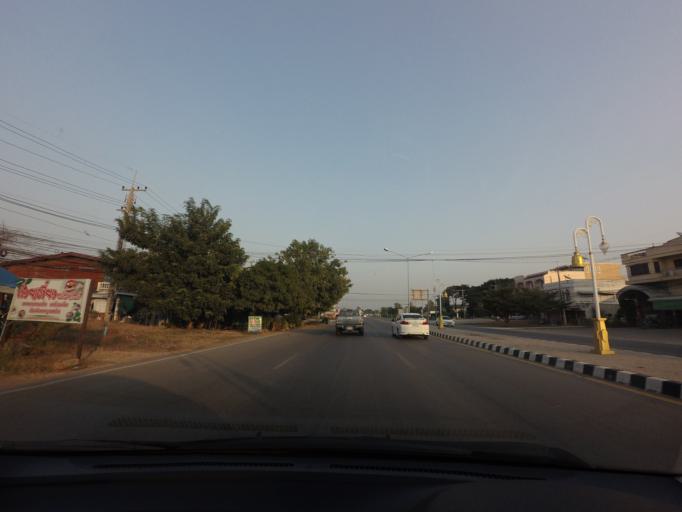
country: TH
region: Sukhothai
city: Sukhothai
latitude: 17.0211
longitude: 99.8221
